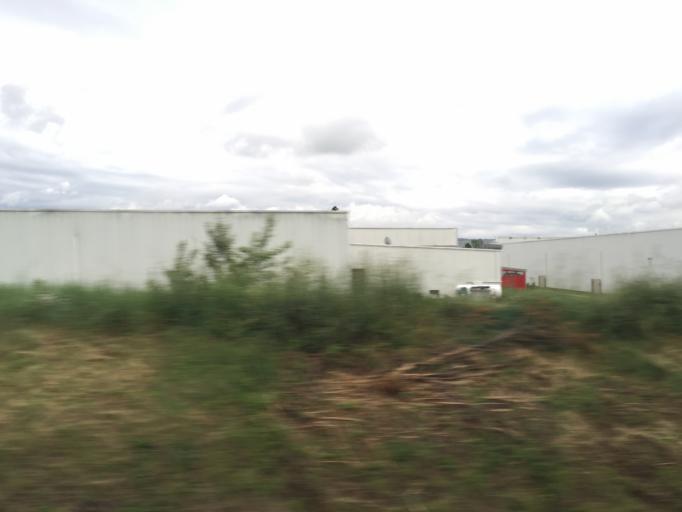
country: FR
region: Rhone-Alpes
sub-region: Departement de la Drome
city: Montelimar
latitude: 44.5308
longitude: 4.7350
